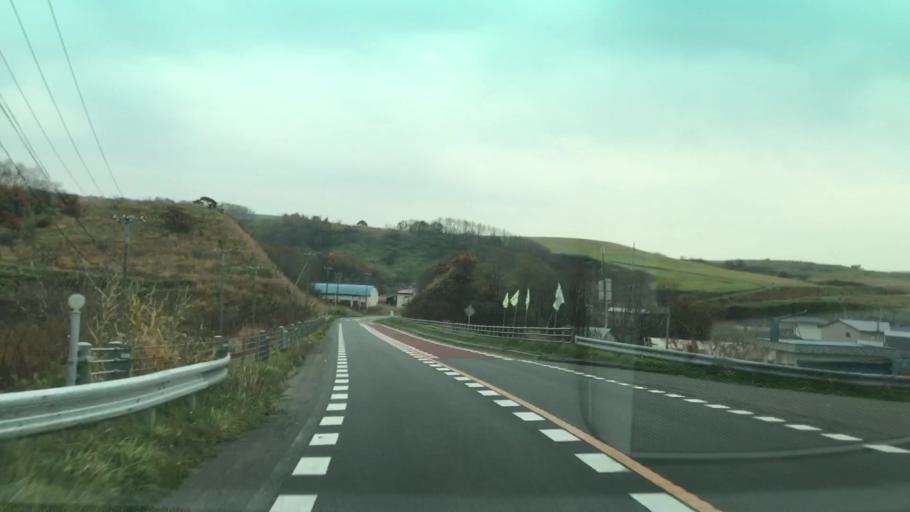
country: JP
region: Hokkaido
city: Ishikari
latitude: 43.3582
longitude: 141.4294
